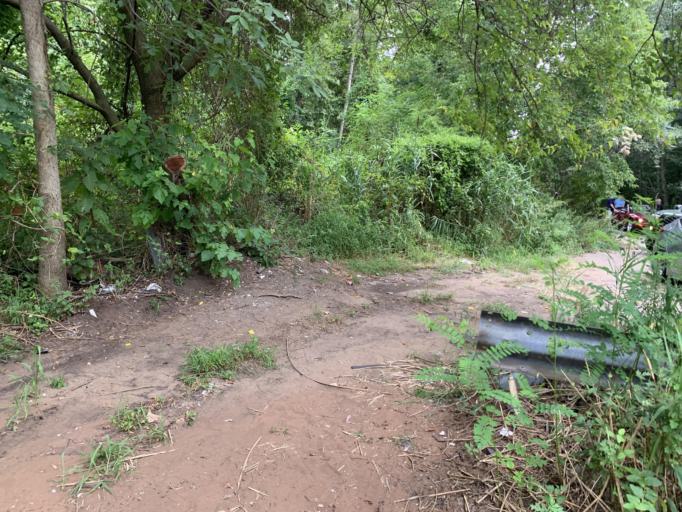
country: US
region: Pennsylvania
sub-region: Delaware County
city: Chester
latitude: 39.8184
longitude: -75.3728
